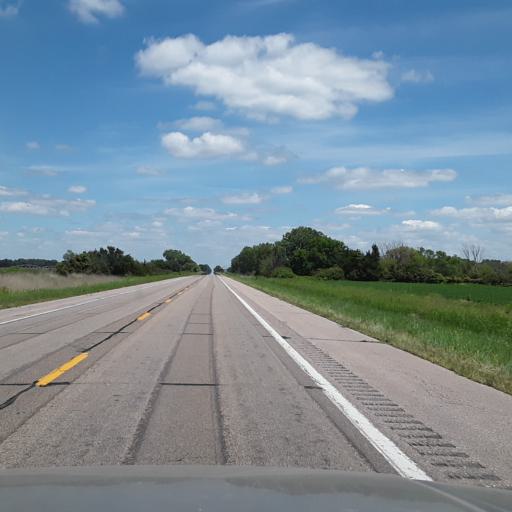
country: US
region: Nebraska
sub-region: Platte County
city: Columbus
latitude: 41.3669
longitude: -97.5435
